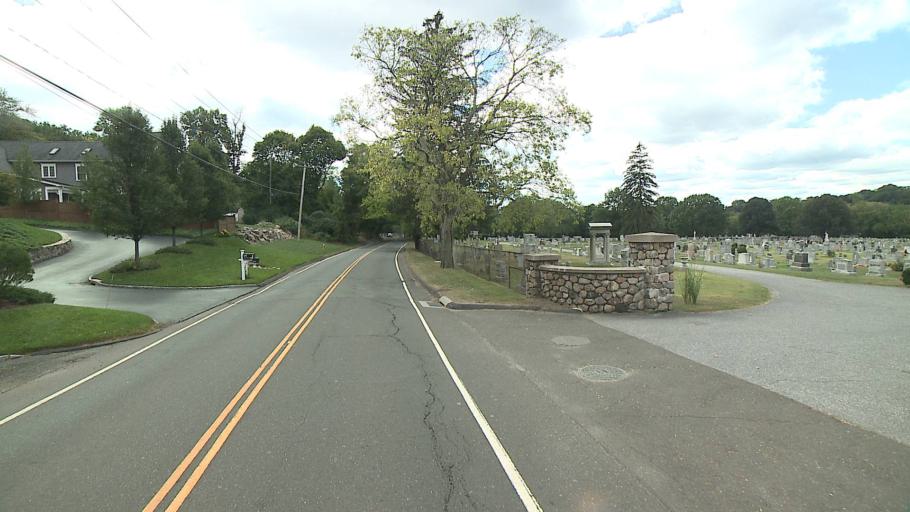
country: US
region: Connecticut
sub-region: Fairfield County
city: Darien
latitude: 41.0912
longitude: -73.5117
